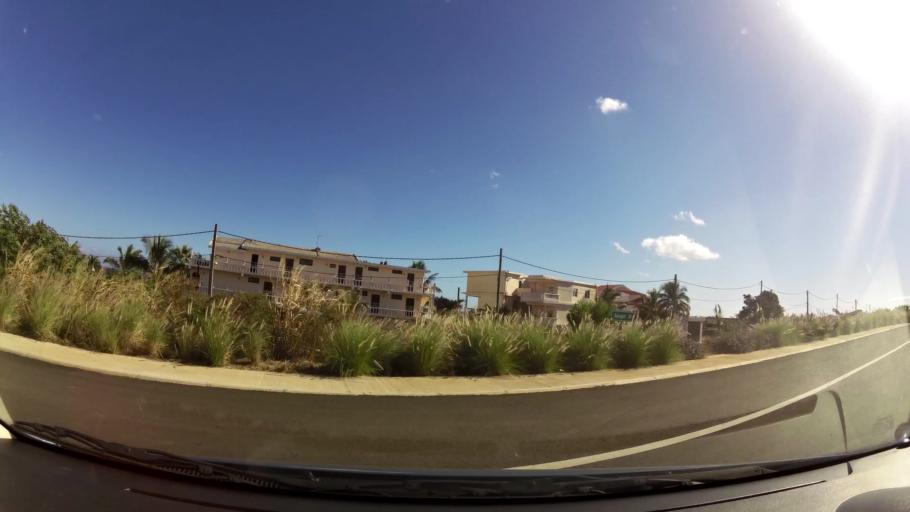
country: MU
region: Black River
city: Flic en Flac
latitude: -20.2653
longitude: 57.3789
